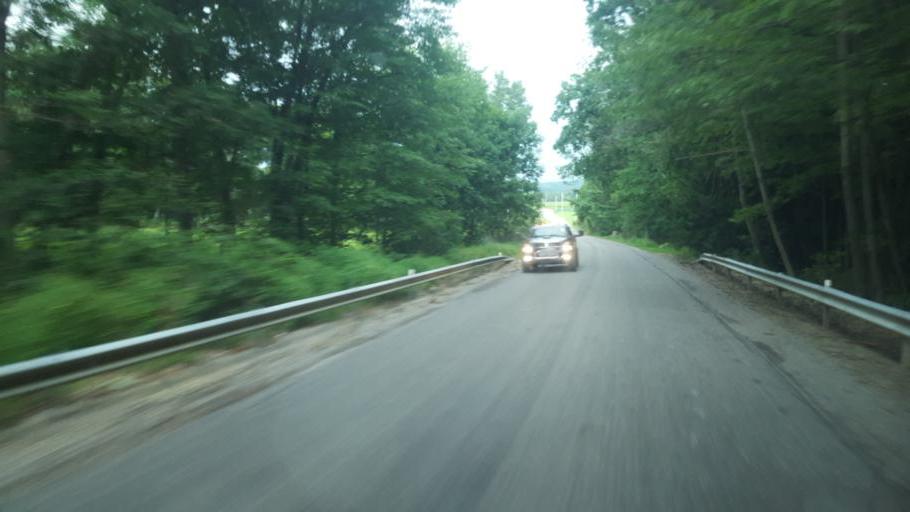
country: US
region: Pennsylvania
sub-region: Clarion County
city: Knox
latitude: 41.1775
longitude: -79.5386
